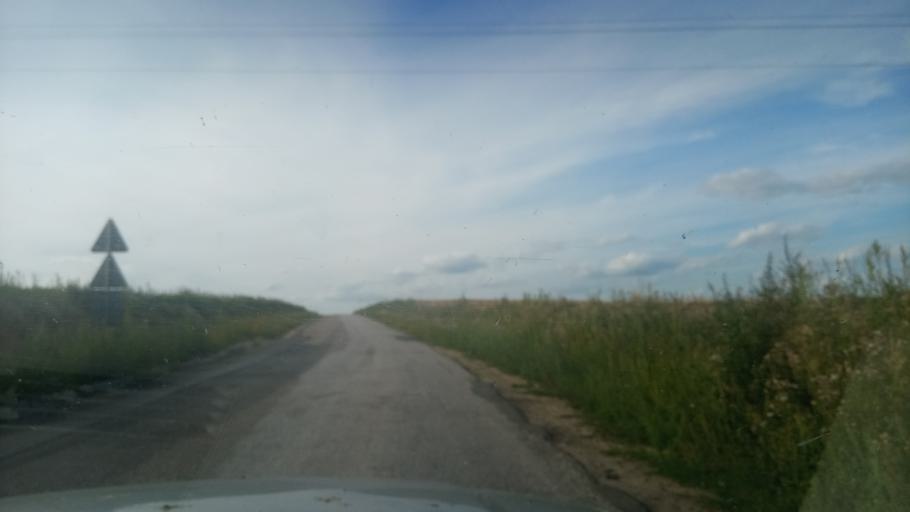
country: PL
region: Kujawsko-Pomorskie
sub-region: Powiat nakielski
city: Sadki
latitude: 53.1974
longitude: 17.3851
